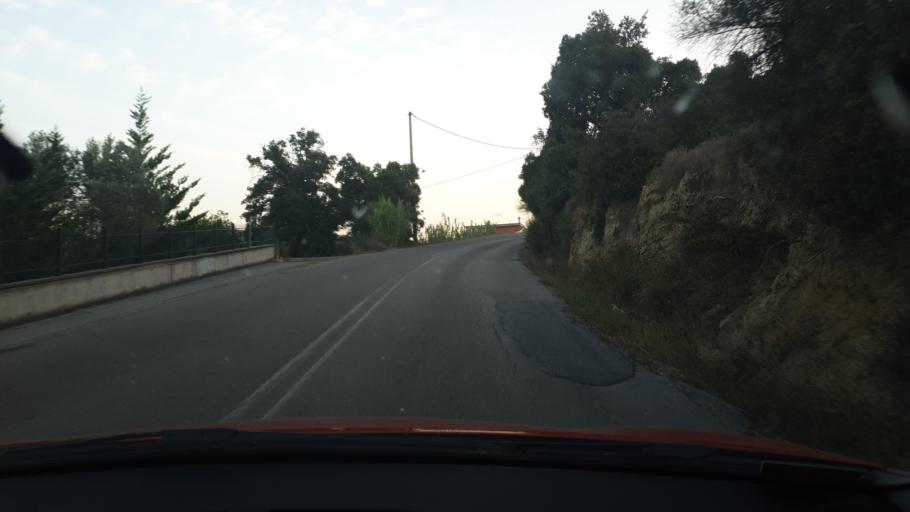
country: GR
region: Central Greece
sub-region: Nomos Evvoias
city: Oxilithos
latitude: 38.5706
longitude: 24.1228
